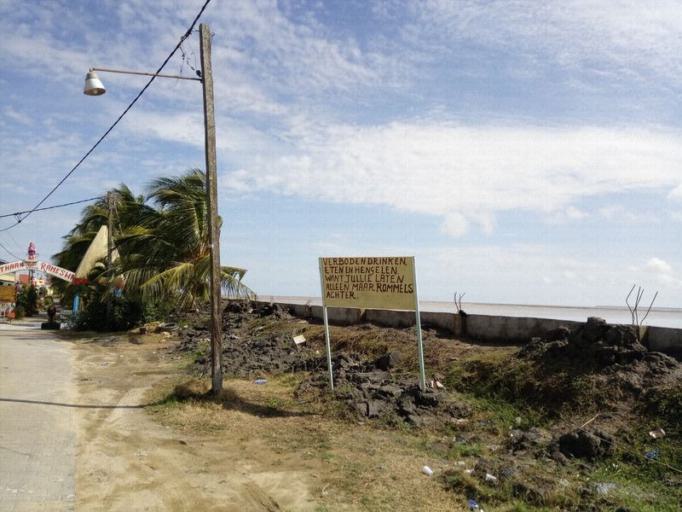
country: SR
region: Paramaribo
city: Paramaribo
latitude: 5.9030
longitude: -55.2258
